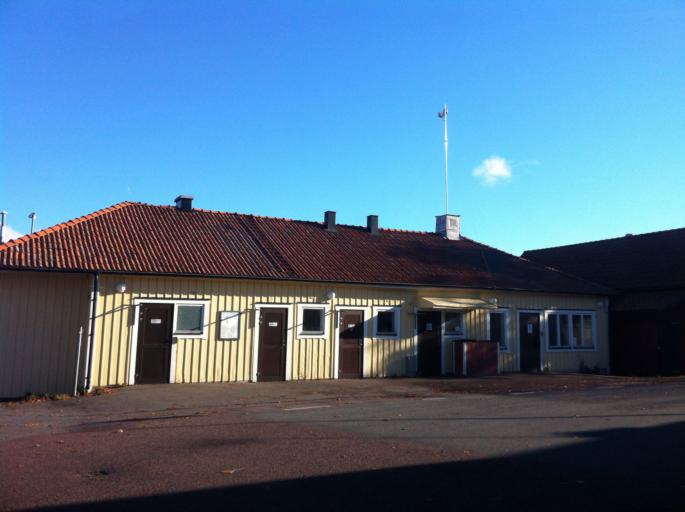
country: SE
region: Uppsala
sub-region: Osthammars Kommun
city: Oregrund
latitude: 60.3407
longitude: 18.4411
